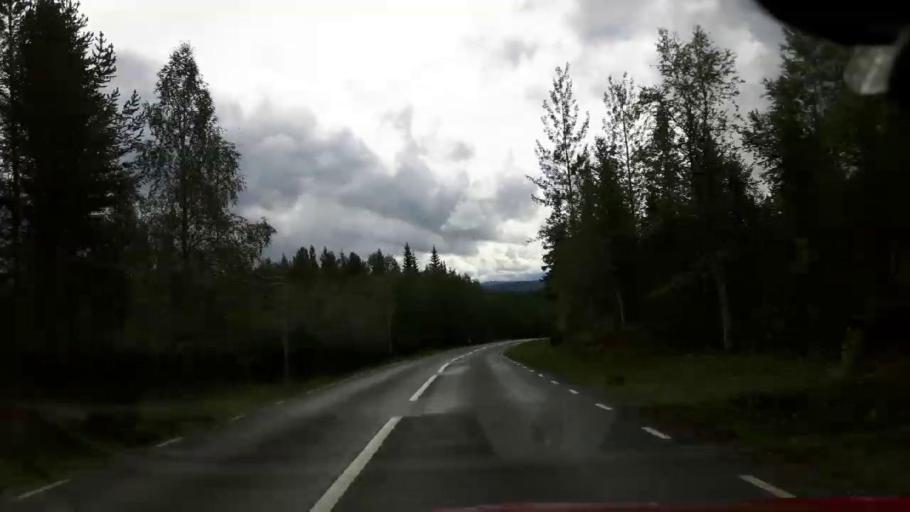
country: NO
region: Nord-Trondelag
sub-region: Lierne
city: Sandvika
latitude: 64.5188
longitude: 14.1621
